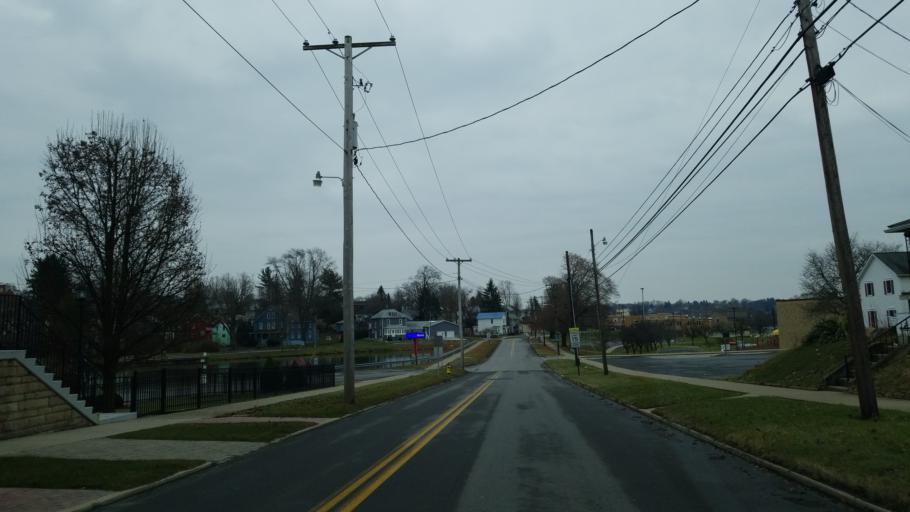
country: US
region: Pennsylvania
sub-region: Clearfield County
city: DuBois
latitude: 41.1327
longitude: -78.7575
